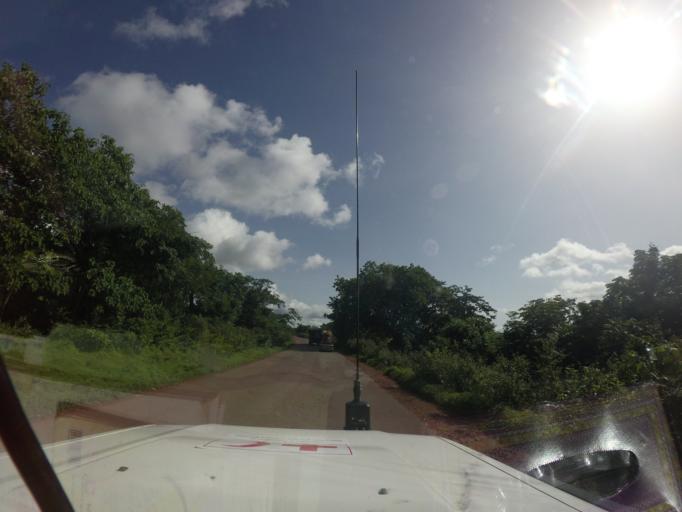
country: GN
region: Mamou
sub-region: Mamou Prefecture
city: Mamou
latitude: 10.2998
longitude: -12.3500
